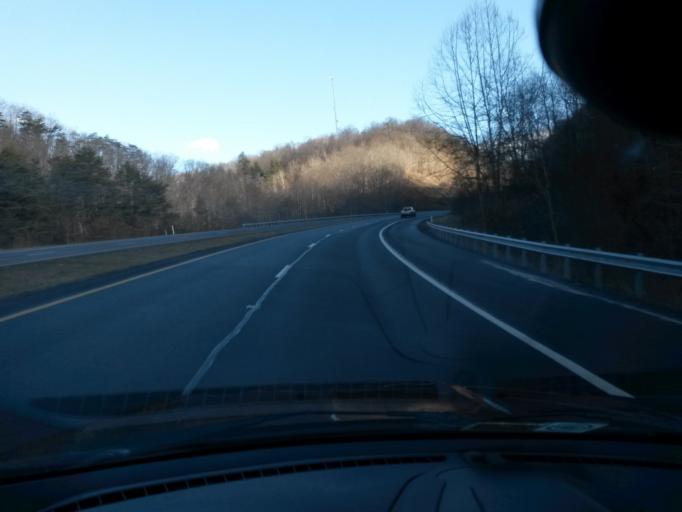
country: US
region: West Virginia
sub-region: Mercer County
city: Athens
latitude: 37.3465
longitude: -80.9440
